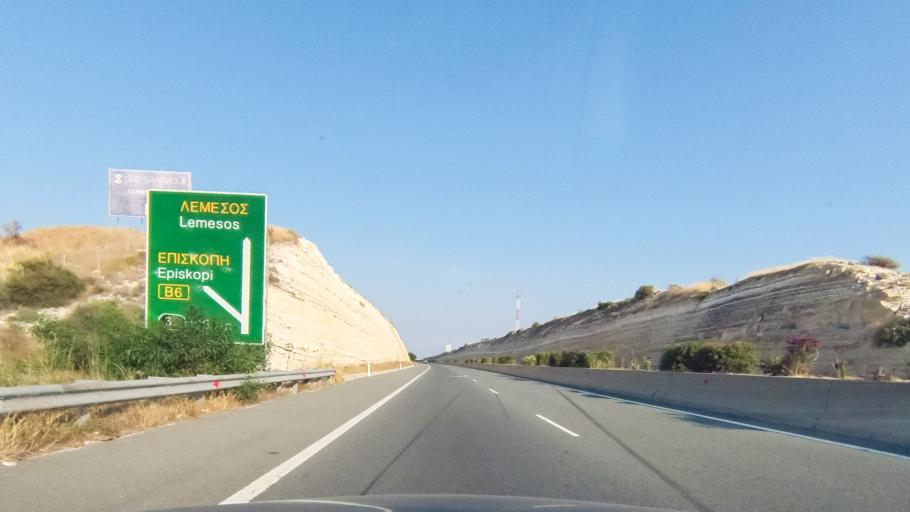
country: CY
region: Limassol
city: Sotira
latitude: 34.6871
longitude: 32.8749
